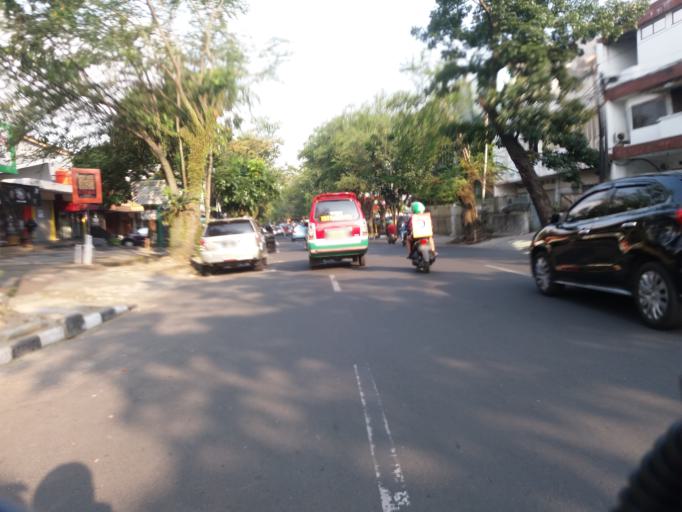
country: ID
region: West Java
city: Bandung
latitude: -6.9255
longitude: 107.6120
